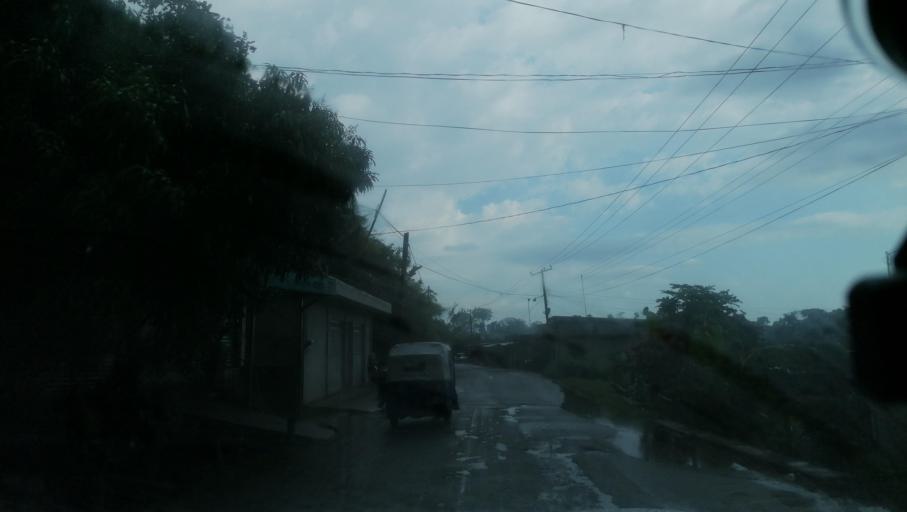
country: MX
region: Chiapas
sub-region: Cacahoatan
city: Benito Juarez
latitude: 15.0543
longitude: -92.1910
